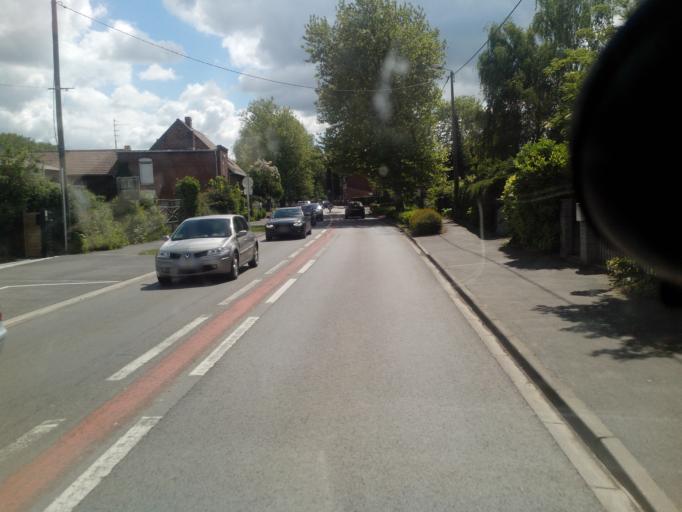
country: FR
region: Nord-Pas-de-Calais
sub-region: Departement du Pas-de-Calais
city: Sailly-sur-la-Lys
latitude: 50.6621
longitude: 2.7856
